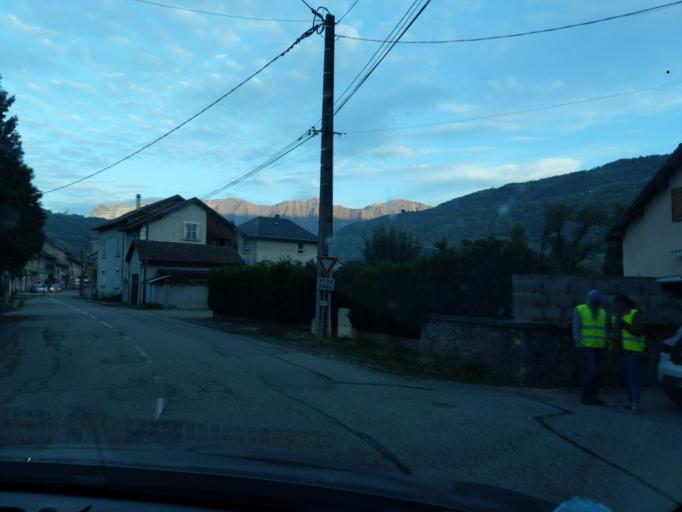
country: FR
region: Rhone-Alpes
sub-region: Departement de la Savoie
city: Aiton
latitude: 45.5408
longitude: 6.3079
